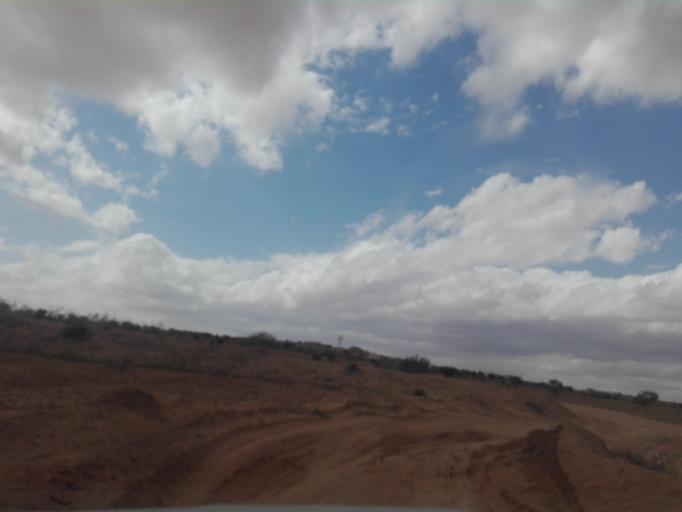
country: TN
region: Safaqis
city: Sfax
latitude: 34.7000
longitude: 10.4419
